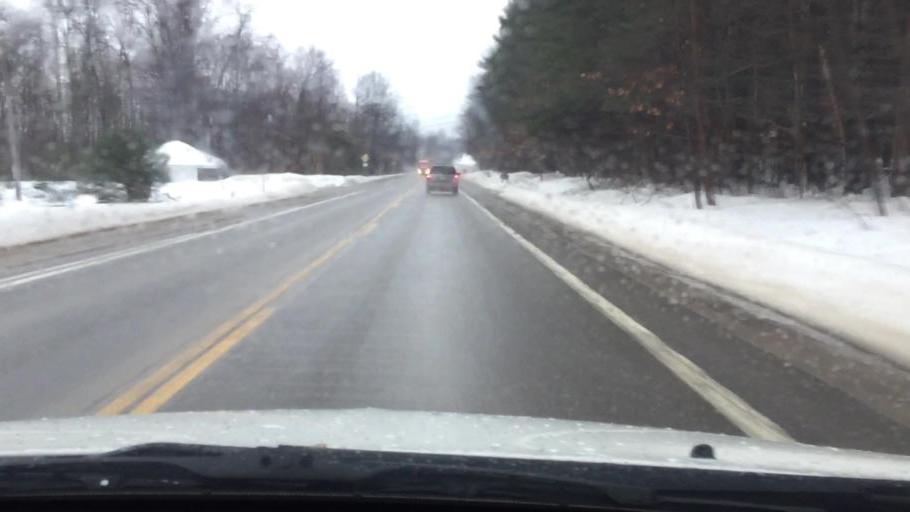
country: US
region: Michigan
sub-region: Charlevoix County
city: East Jordan
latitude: 45.2036
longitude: -85.1651
